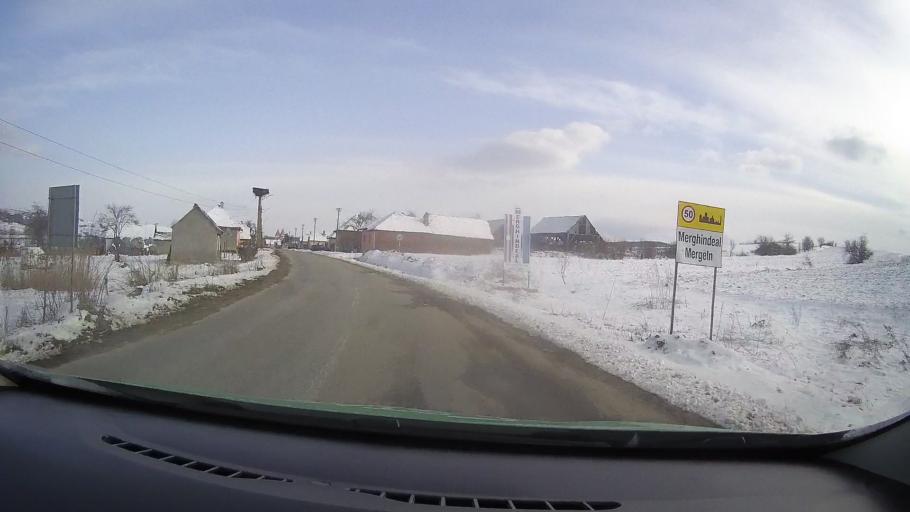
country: RO
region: Sibiu
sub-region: Comuna Merghindeal
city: Merghindeal
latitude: 45.9678
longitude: 24.7123
